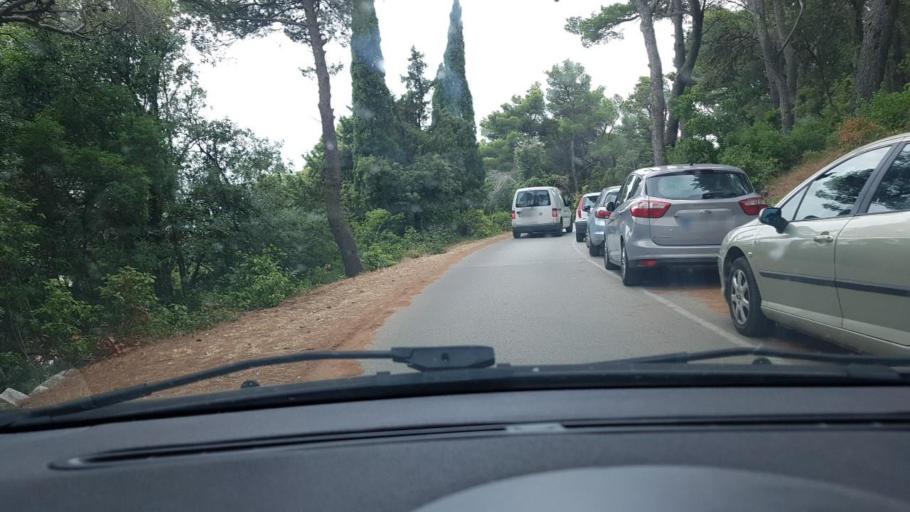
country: HR
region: Dubrovacko-Neretvanska
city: Korcula
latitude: 42.9592
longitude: 17.1324
